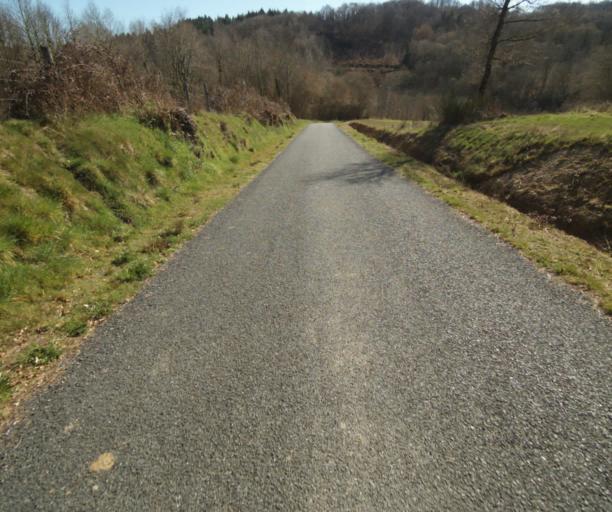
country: FR
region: Limousin
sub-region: Departement de la Correze
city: Chamboulive
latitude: 45.4203
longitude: 1.6477
